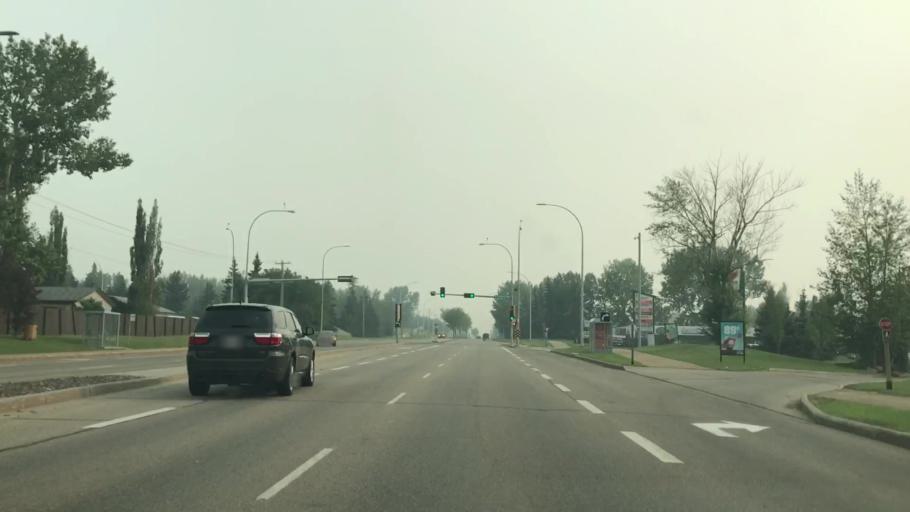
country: CA
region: Alberta
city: Sherwood Park
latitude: 53.5355
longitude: -113.3202
